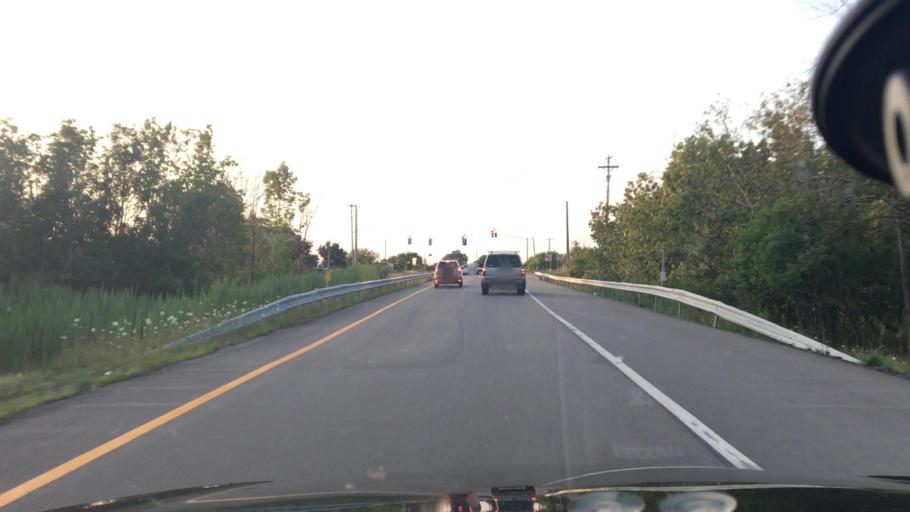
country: US
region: New York
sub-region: Erie County
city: West Seneca
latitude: 42.8273
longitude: -78.7875
